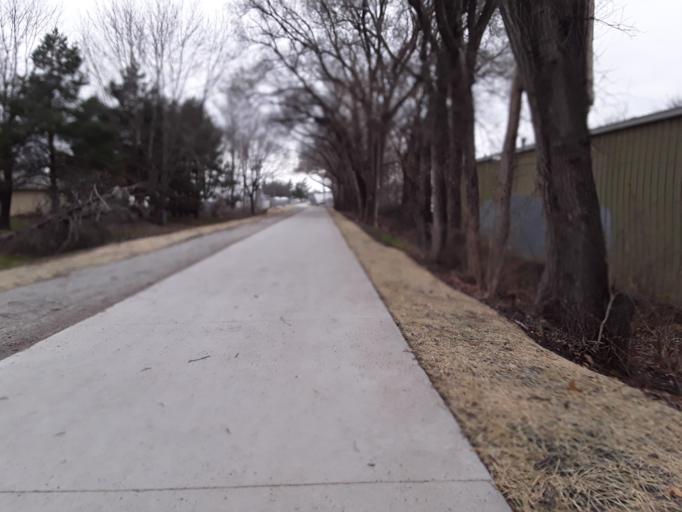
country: US
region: Nebraska
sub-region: Lancaster County
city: Lincoln
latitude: 40.8514
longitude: -96.6364
